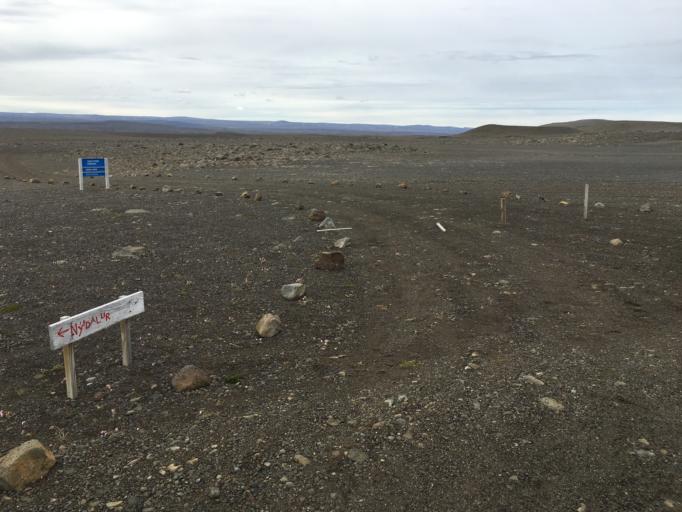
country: IS
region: Northeast
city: Laugar
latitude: 64.9995
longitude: -17.4380
